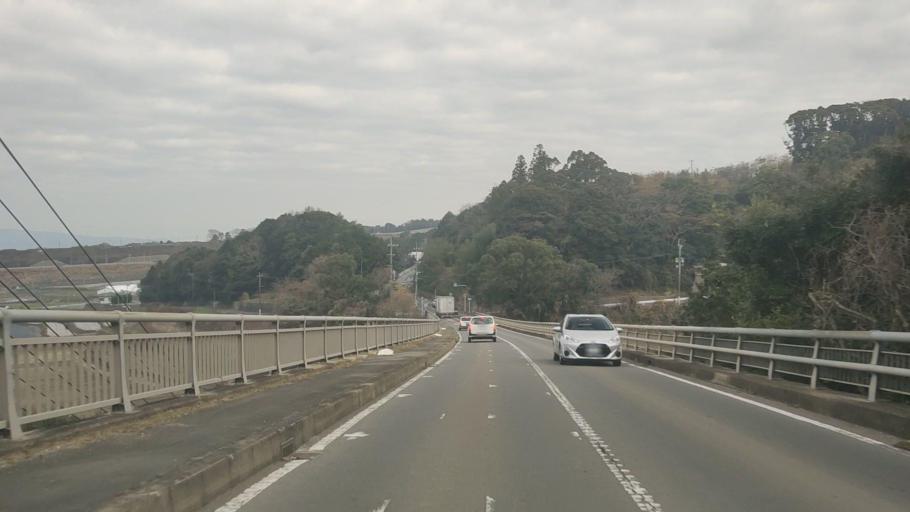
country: JP
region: Nagasaki
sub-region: Isahaya-shi
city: Isahaya
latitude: 32.8115
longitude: 130.1716
